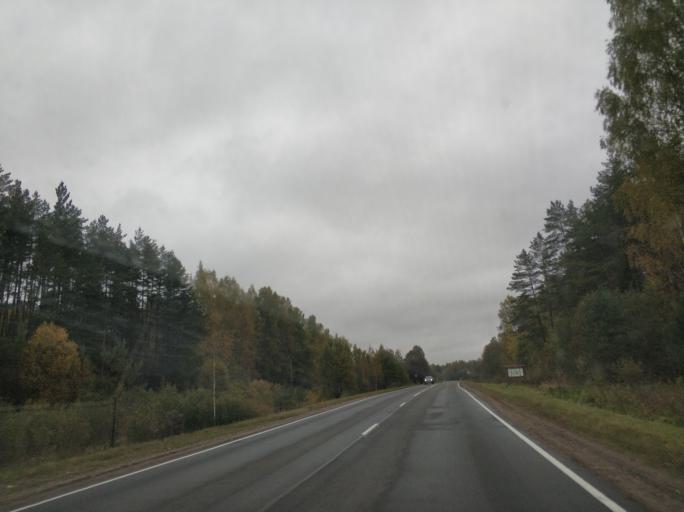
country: BY
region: Vitebsk
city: Rasony
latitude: 56.0960
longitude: 28.7224
